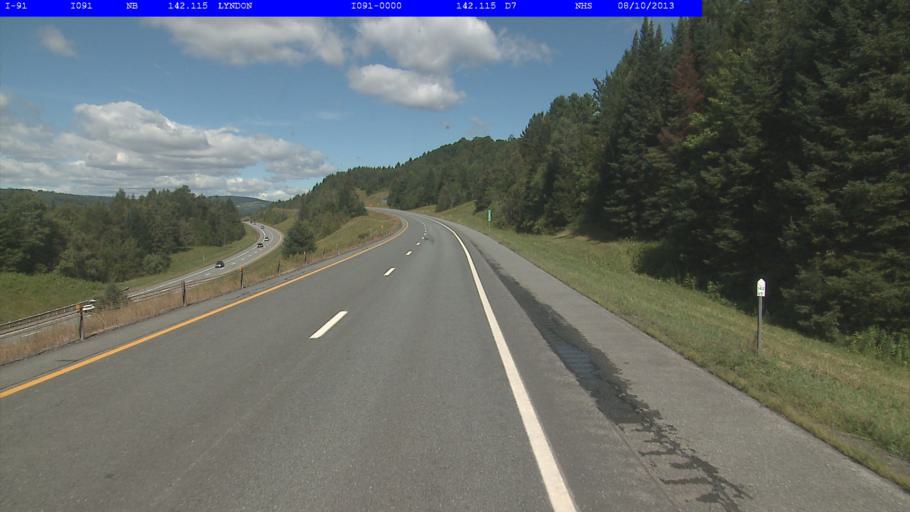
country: US
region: Vermont
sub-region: Caledonia County
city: Lyndonville
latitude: 44.5787
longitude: -72.0506
